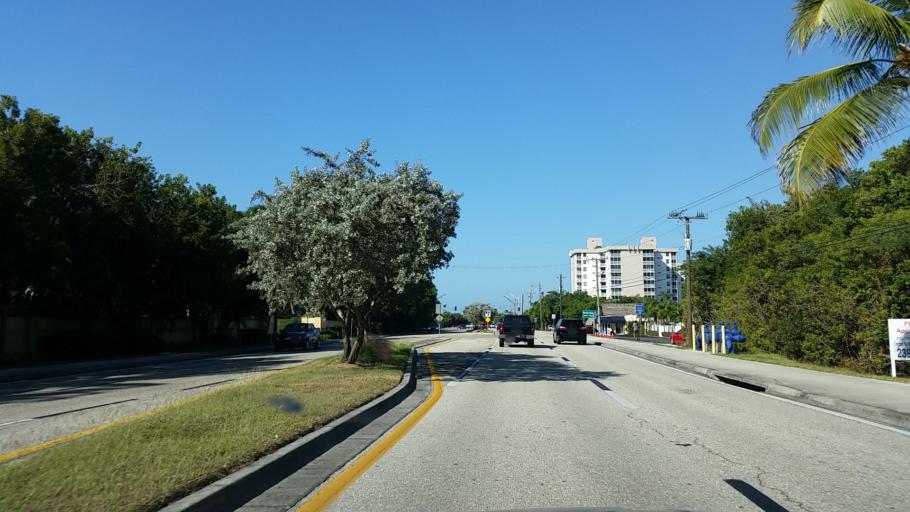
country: US
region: Florida
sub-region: Lee County
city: Bonita Springs
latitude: 26.3304
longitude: -81.8398
